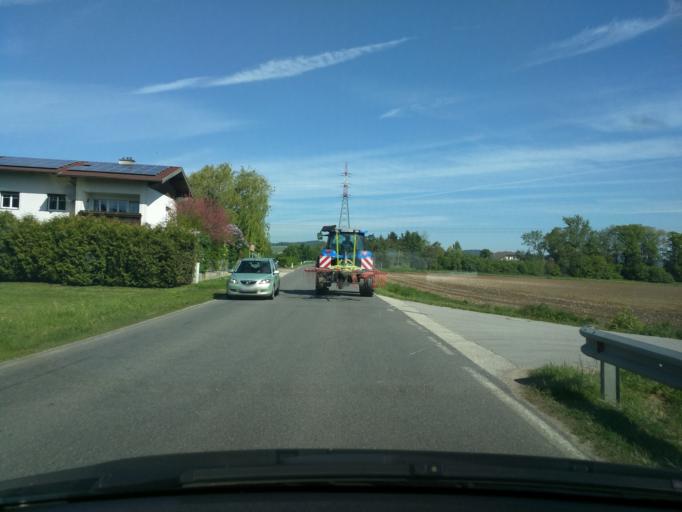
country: AT
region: Lower Austria
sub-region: Politischer Bezirk Amstetten
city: Sankt Georgen am Ybbsfelde
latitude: 48.1133
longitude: 14.9630
